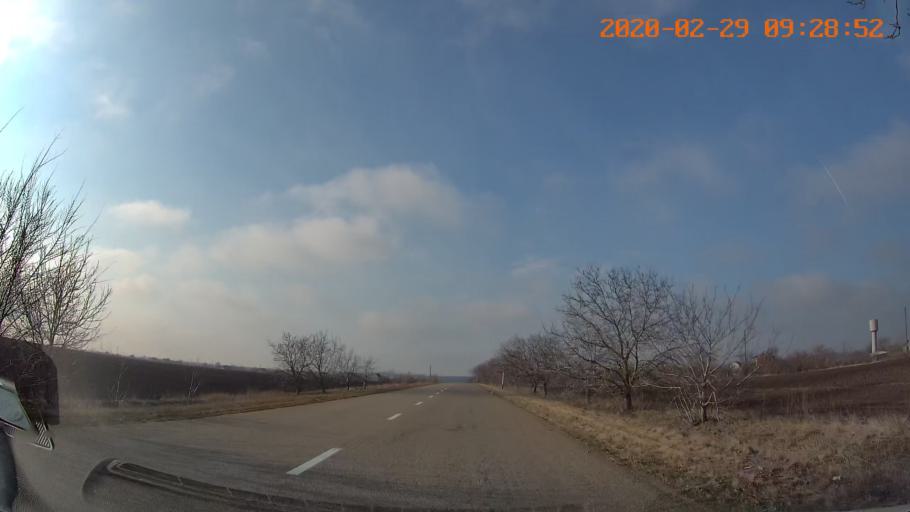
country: UA
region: Odessa
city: Lymanske
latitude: 46.6842
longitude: 29.9256
